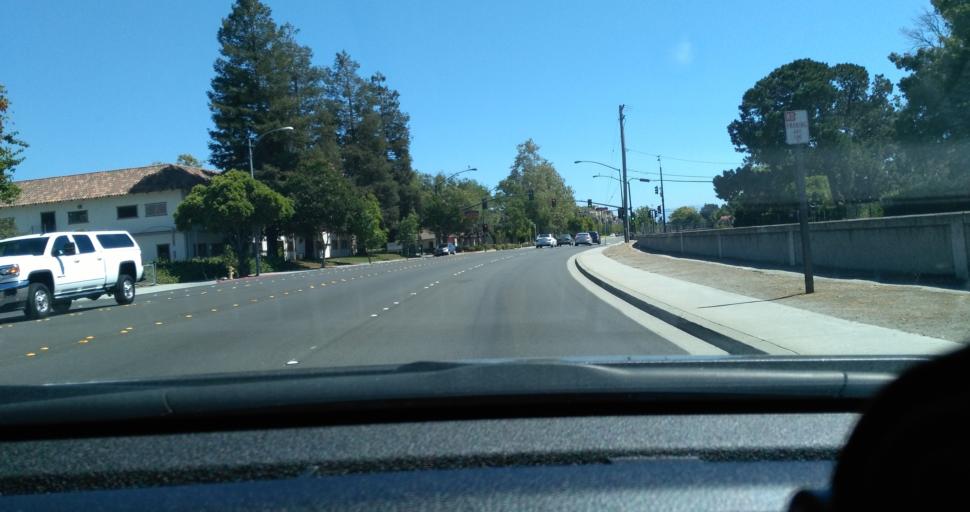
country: US
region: California
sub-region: Santa Clara County
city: Milpitas
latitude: 37.4257
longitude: -121.9077
